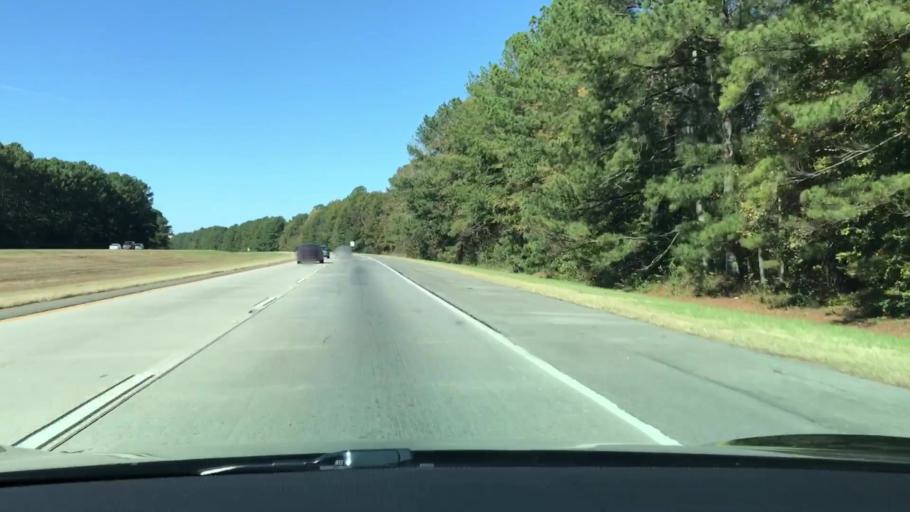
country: US
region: Georgia
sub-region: Taliaferro County
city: Crawfordville
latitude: 33.5363
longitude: -82.9951
